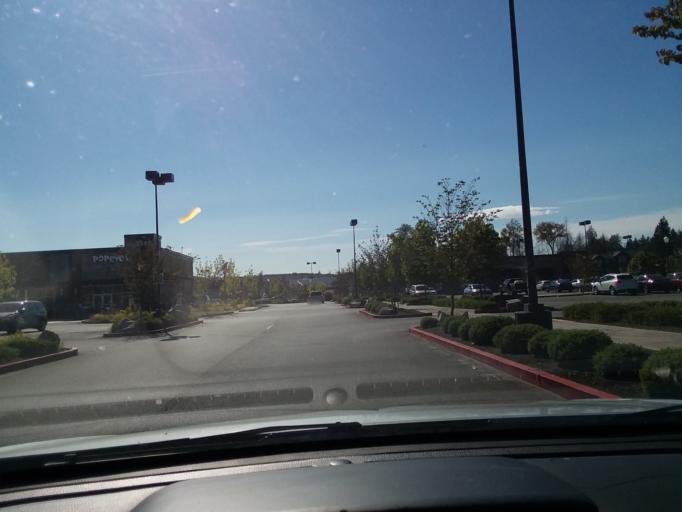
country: US
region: Washington
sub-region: Snohomish County
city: Smokey Point
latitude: 48.1533
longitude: -122.1952
